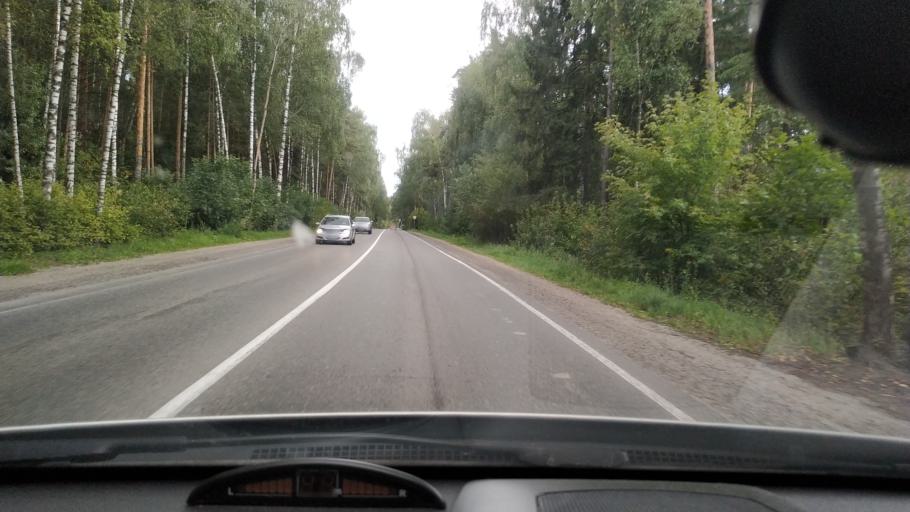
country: RU
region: Moskovskaya
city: Chornaya
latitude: 55.7804
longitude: 38.0418
